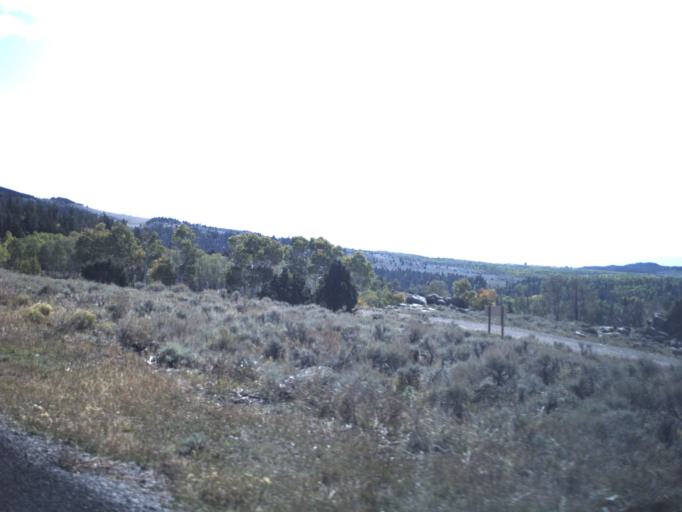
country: US
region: Utah
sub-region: Wayne County
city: Loa
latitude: 38.5133
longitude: -111.7706
